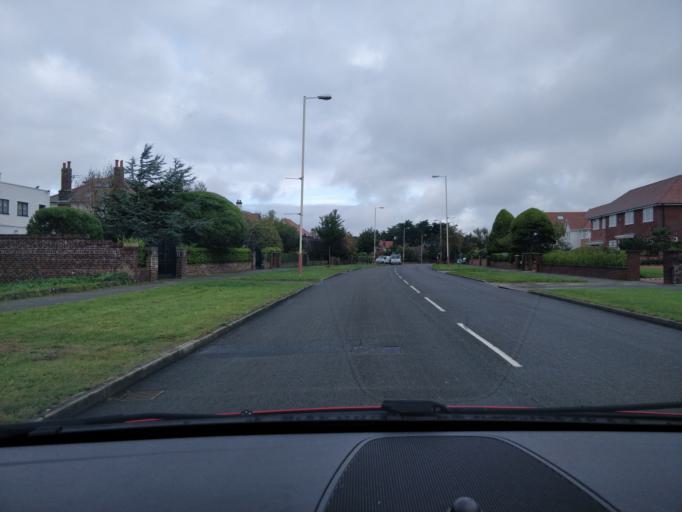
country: GB
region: England
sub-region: Sefton
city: Southport
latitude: 53.6267
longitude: -3.0281
